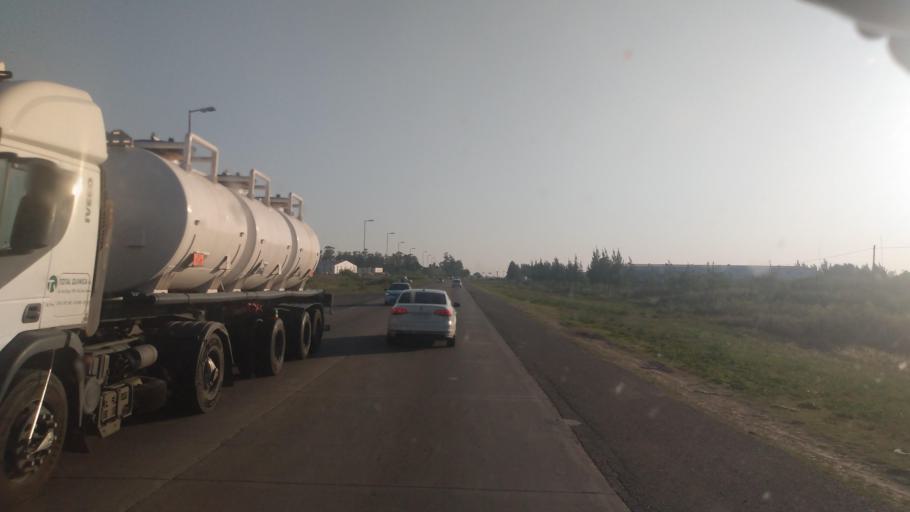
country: AR
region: Buenos Aires
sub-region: Partido de Campana
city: Campana
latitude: -34.1962
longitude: -58.9530
